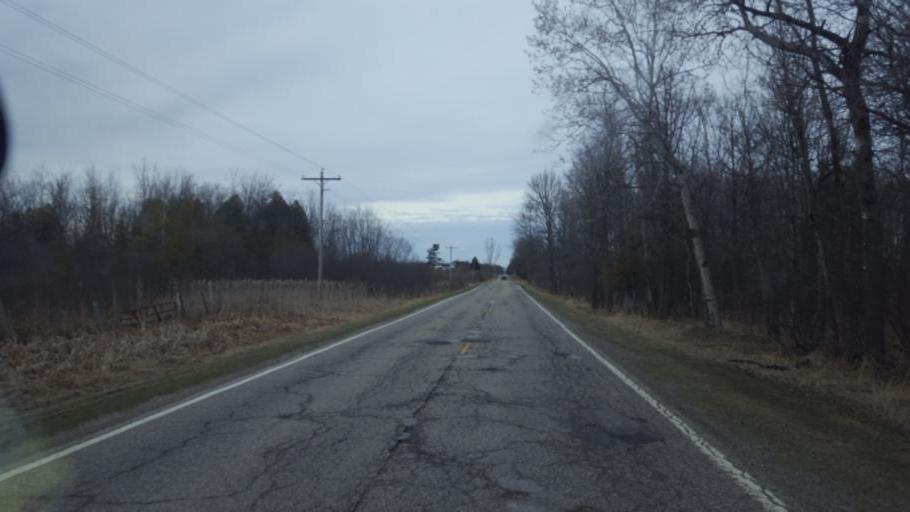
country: US
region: Michigan
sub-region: Montcalm County
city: Edmore
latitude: 43.4804
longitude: -85.0053
